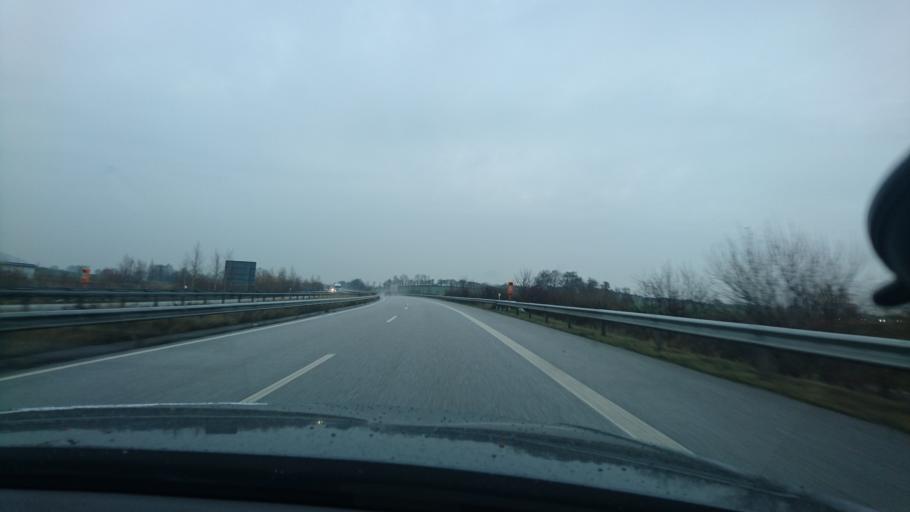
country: DE
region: Schleswig-Holstein
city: Oldenburg in Holstein
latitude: 54.3075
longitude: 10.9059
